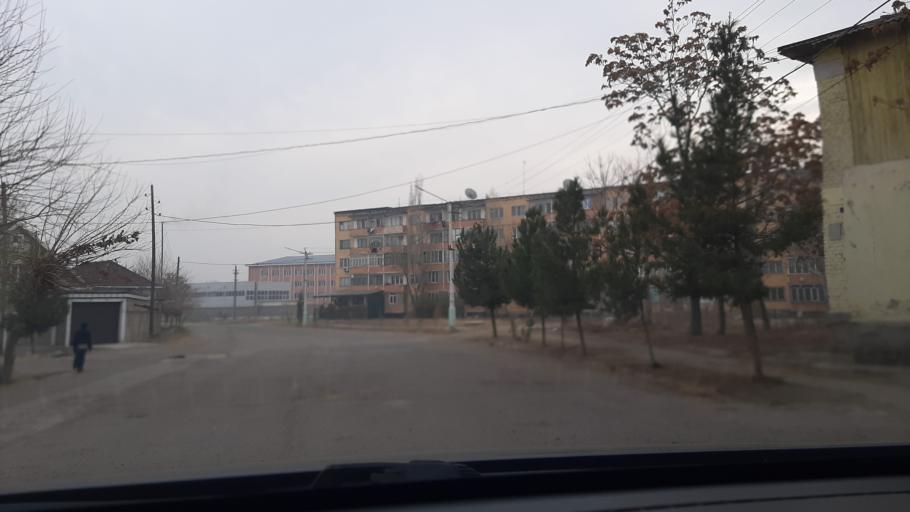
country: TJ
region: Viloyati Sughd
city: Palos
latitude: 40.2622
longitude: 69.7916
